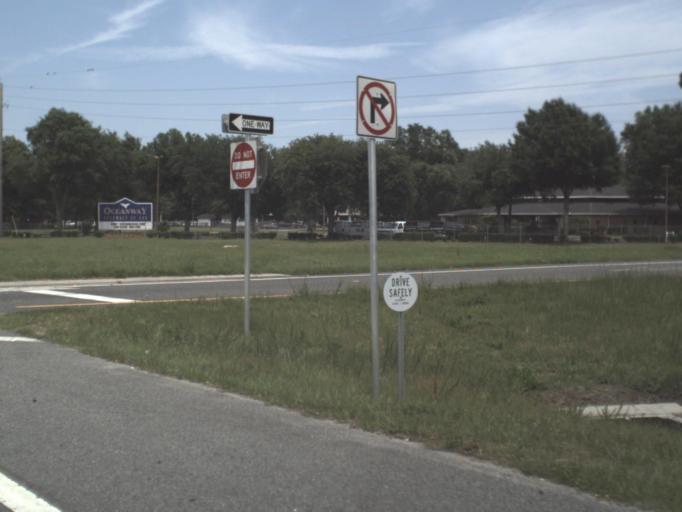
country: US
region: Florida
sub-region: Duval County
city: Jacksonville
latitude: 30.4590
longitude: -81.6353
